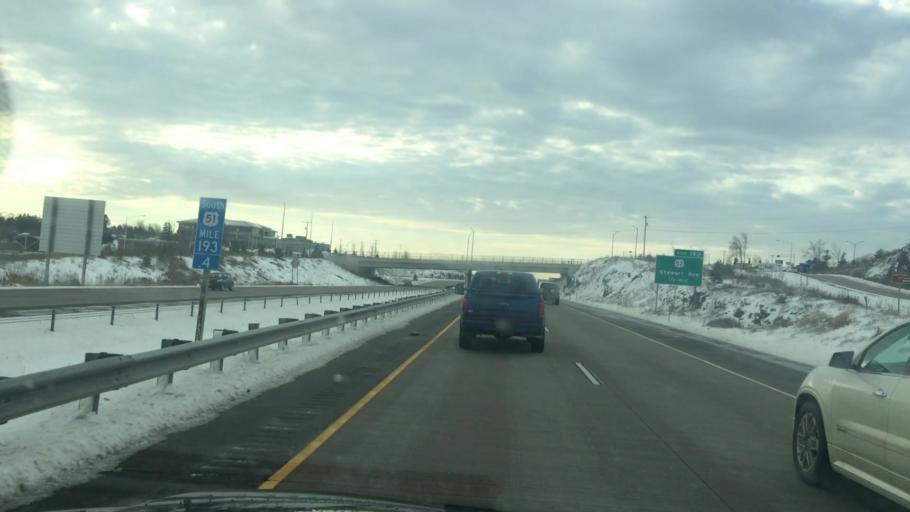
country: US
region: Wisconsin
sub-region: Marathon County
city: Wausau
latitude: 44.9721
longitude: -89.6567
